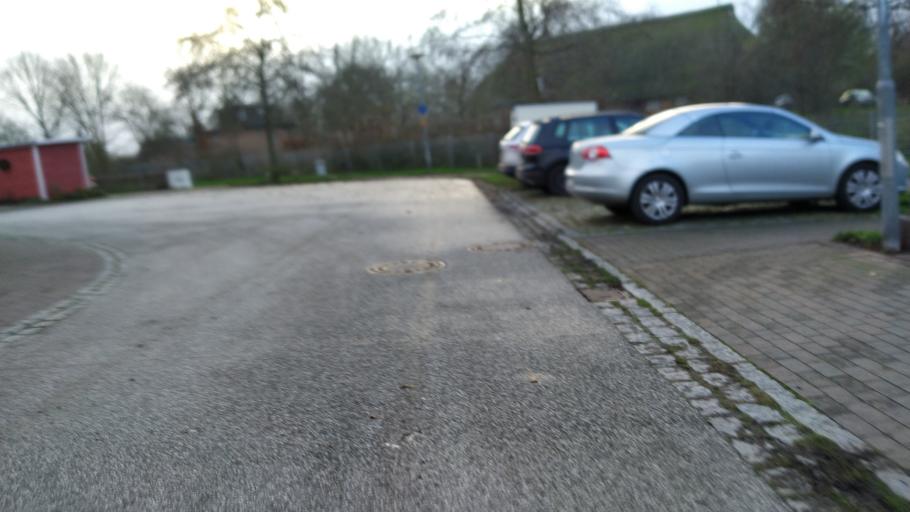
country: DE
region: Schleswig-Holstein
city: Travemuende
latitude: 53.9684
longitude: 10.8575
